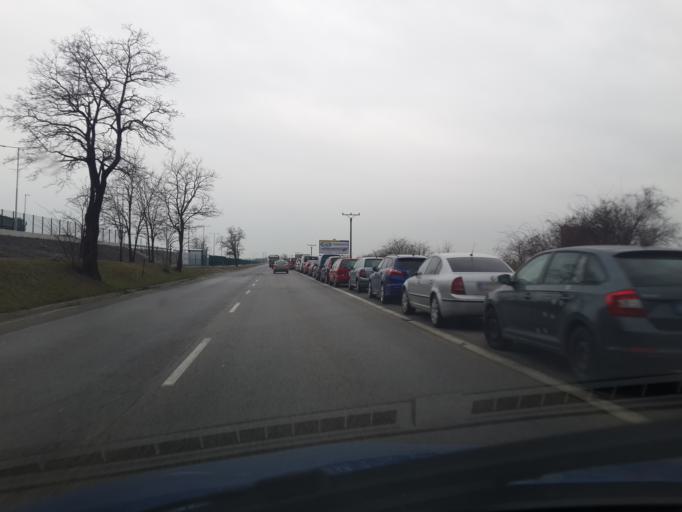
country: SK
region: Bratislavsky
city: Stupava
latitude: 48.2321
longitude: 16.9978
